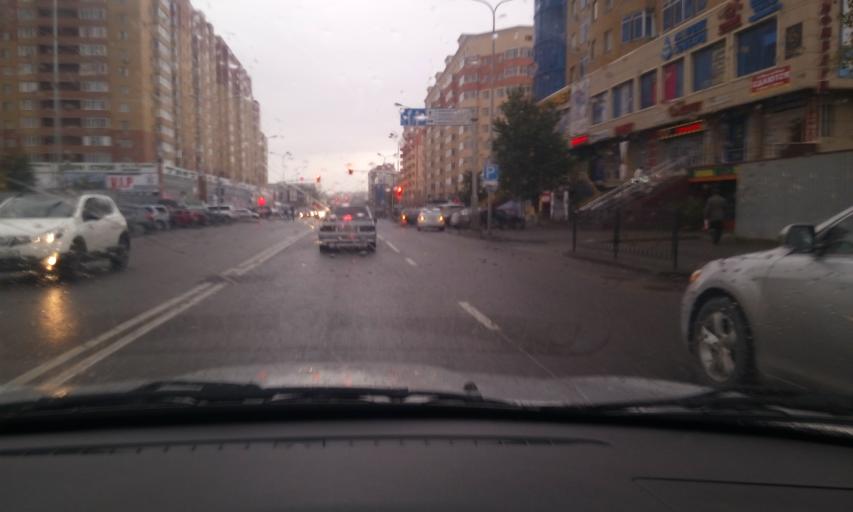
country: KZ
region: Astana Qalasy
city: Astana
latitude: 51.1622
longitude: 71.4546
